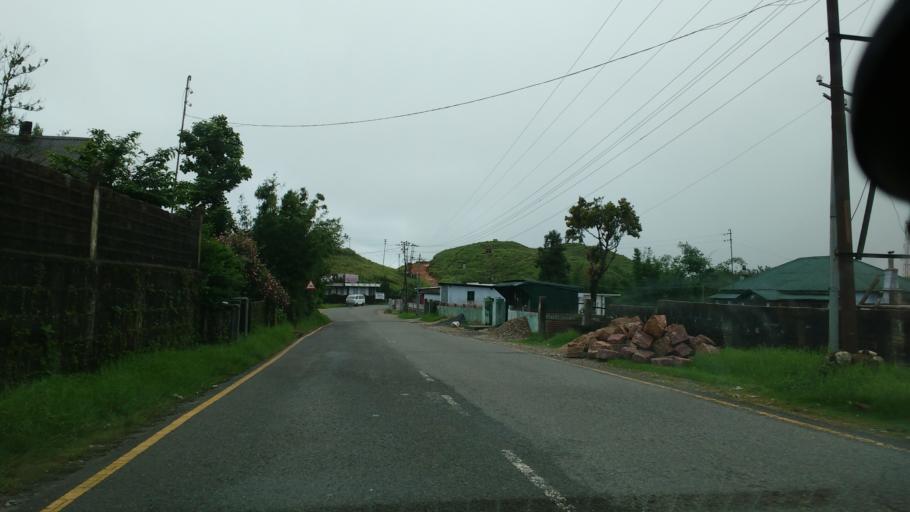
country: IN
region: Meghalaya
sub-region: East Khasi Hills
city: Cherrapunji
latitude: 25.2750
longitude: 91.7307
